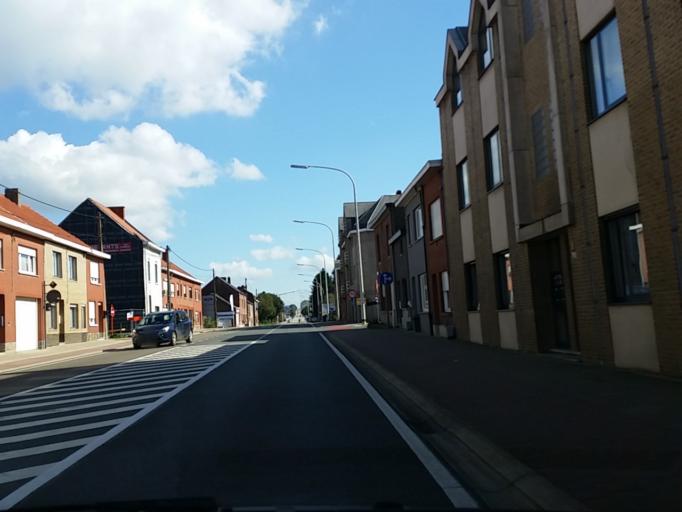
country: BE
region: Flanders
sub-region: Provincie Vlaams-Brabant
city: Holsbeek
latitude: 50.8896
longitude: 4.7691
